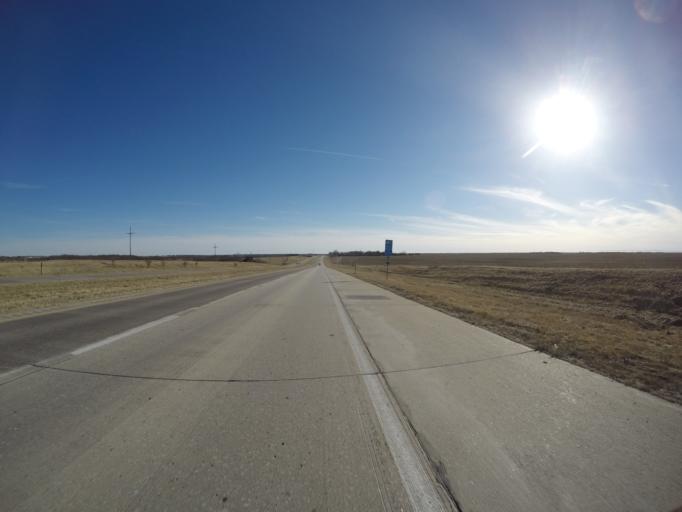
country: US
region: Nebraska
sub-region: Gage County
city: Beatrice
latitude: 40.3348
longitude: -96.7468
